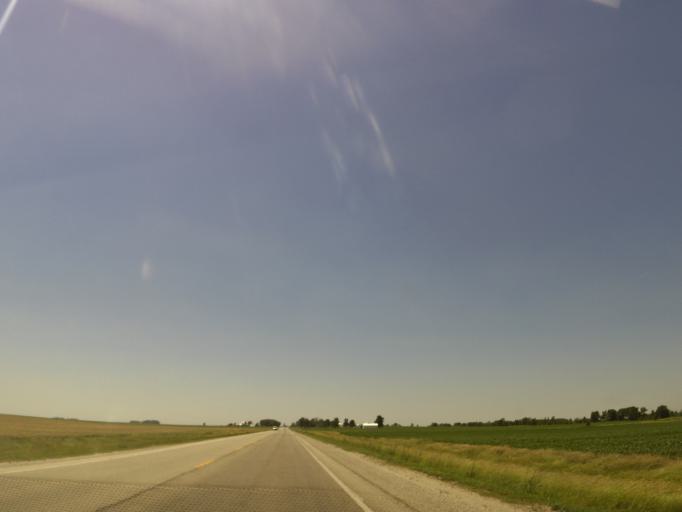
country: US
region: Illinois
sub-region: Livingston County
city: Fairbury
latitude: 40.7439
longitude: -88.5454
